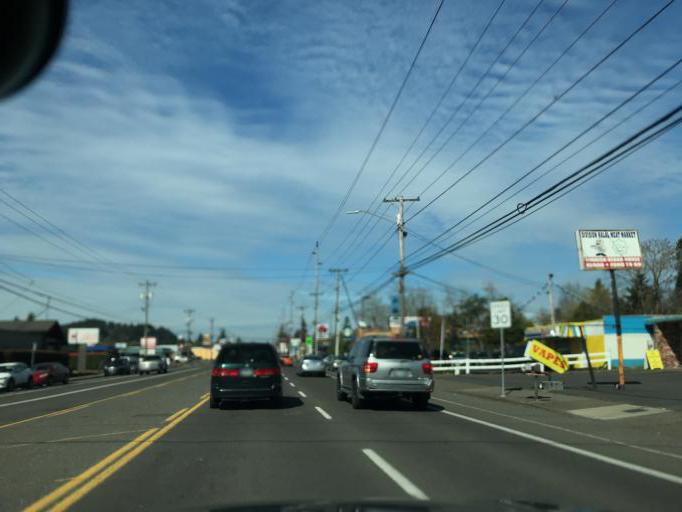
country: US
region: Oregon
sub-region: Multnomah County
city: Lents
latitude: 45.5041
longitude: -122.5323
